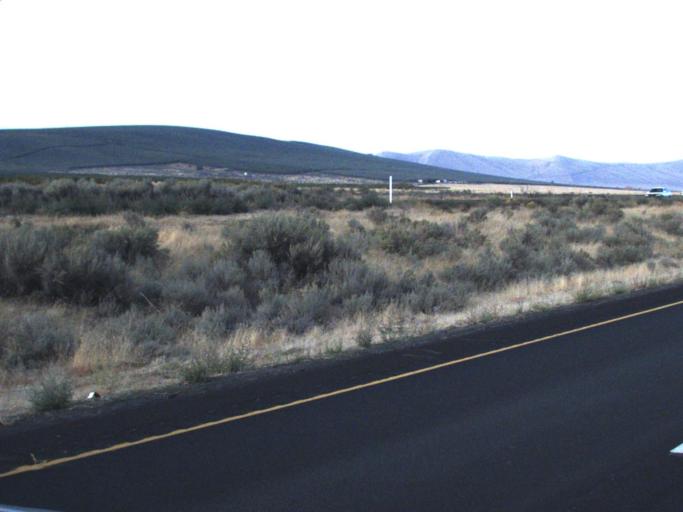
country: US
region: Washington
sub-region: Benton County
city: West Richland
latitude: 46.2620
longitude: -119.3988
